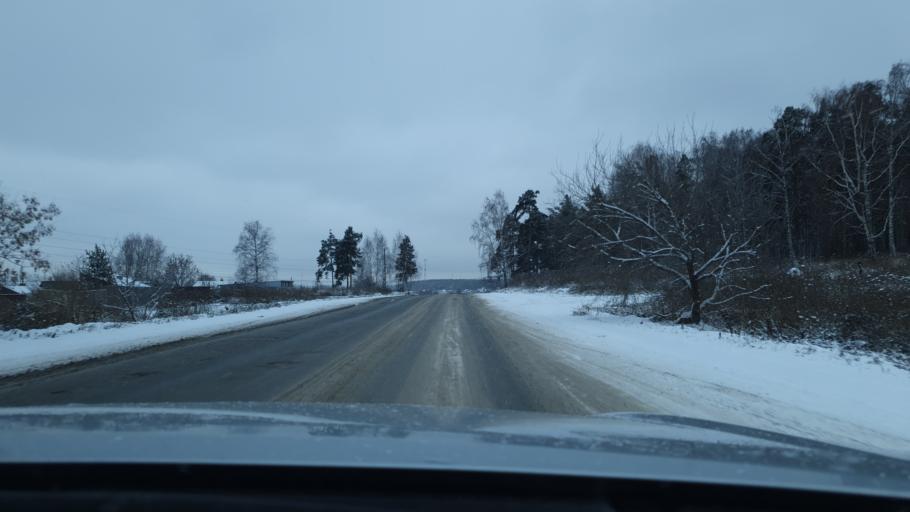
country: RU
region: Sverdlovsk
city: Istok
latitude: 56.7781
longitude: 60.7398
